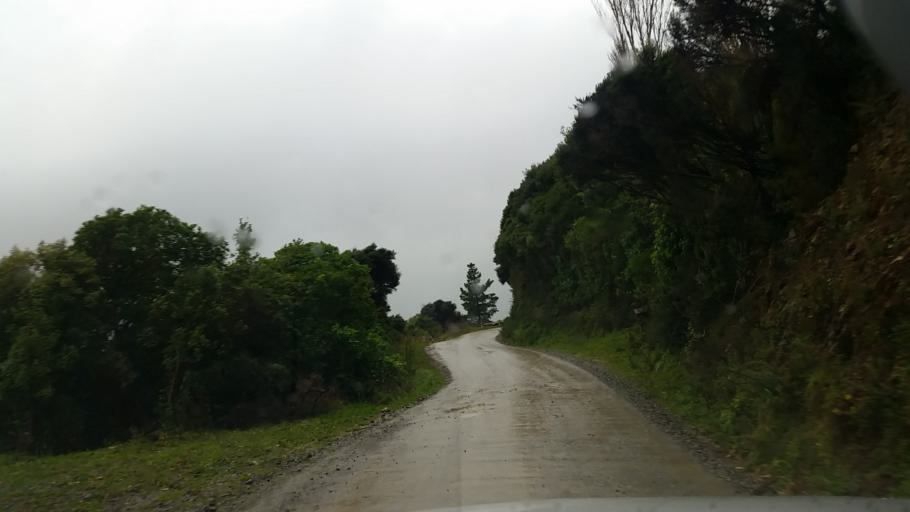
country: NZ
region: Marlborough
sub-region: Marlborough District
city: Picton
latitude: -41.1721
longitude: 174.0417
